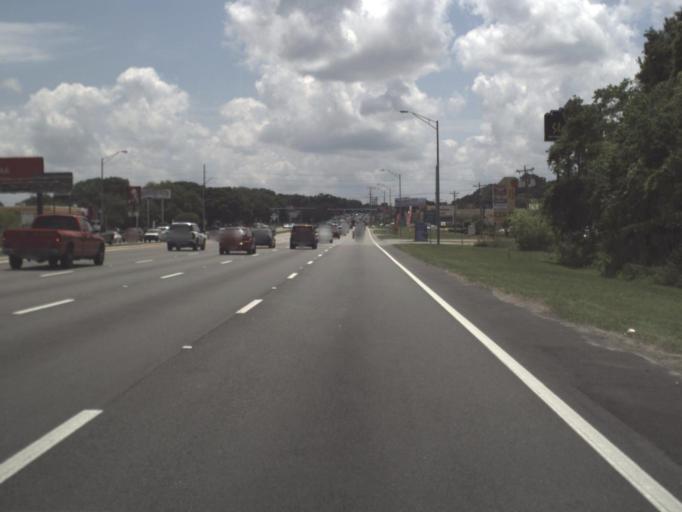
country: US
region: Florida
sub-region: Clay County
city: Bellair-Meadowbrook Terrace
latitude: 30.1904
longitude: -81.7395
